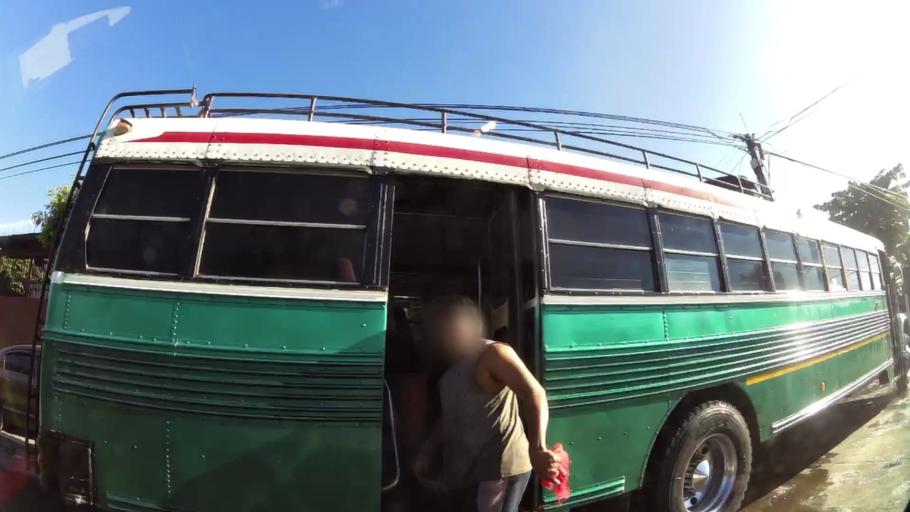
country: SV
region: Sonsonate
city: Sonsonate
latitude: 13.7143
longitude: -89.7162
